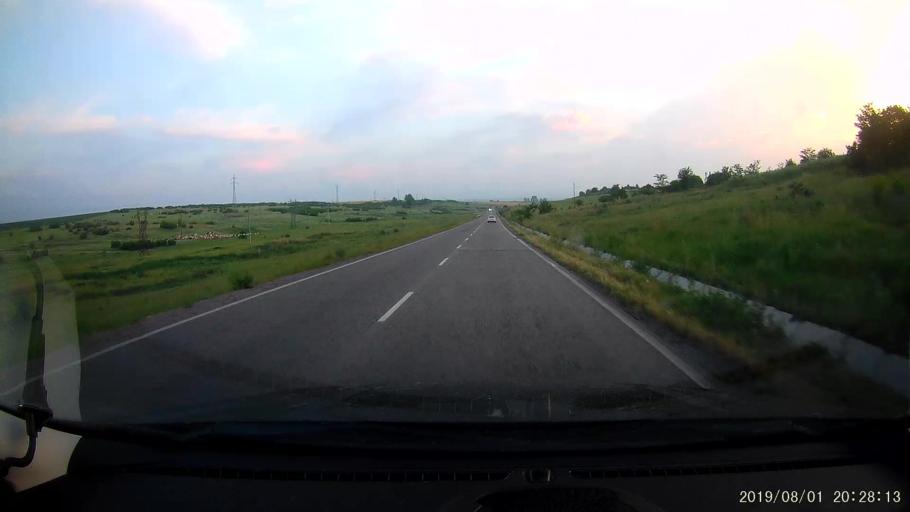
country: BG
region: Yambol
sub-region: Obshtina Elkhovo
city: Elkhovo
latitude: 42.1708
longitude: 26.5802
